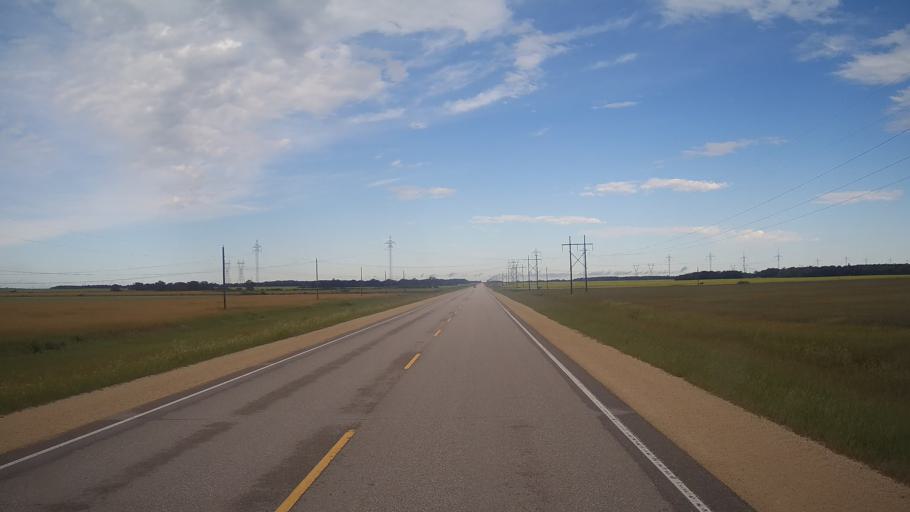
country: CA
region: Manitoba
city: Stonewall
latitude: 50.1226
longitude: -97.4770
